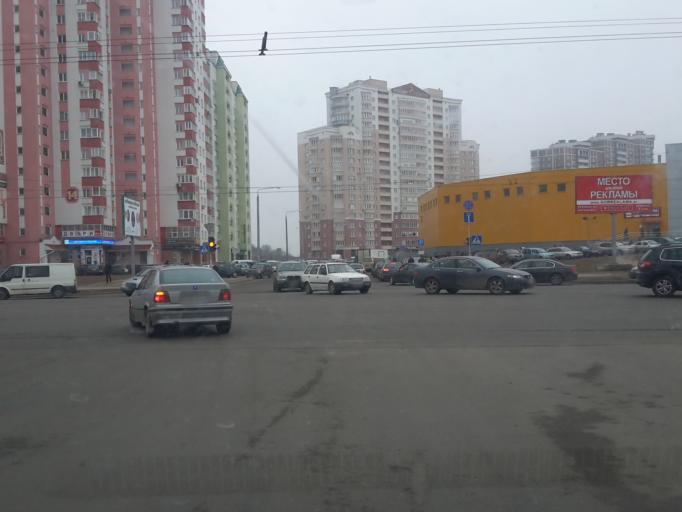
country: BY
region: Minsk
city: Novoye Medvezhino
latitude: 53.9049
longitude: 27.4360
